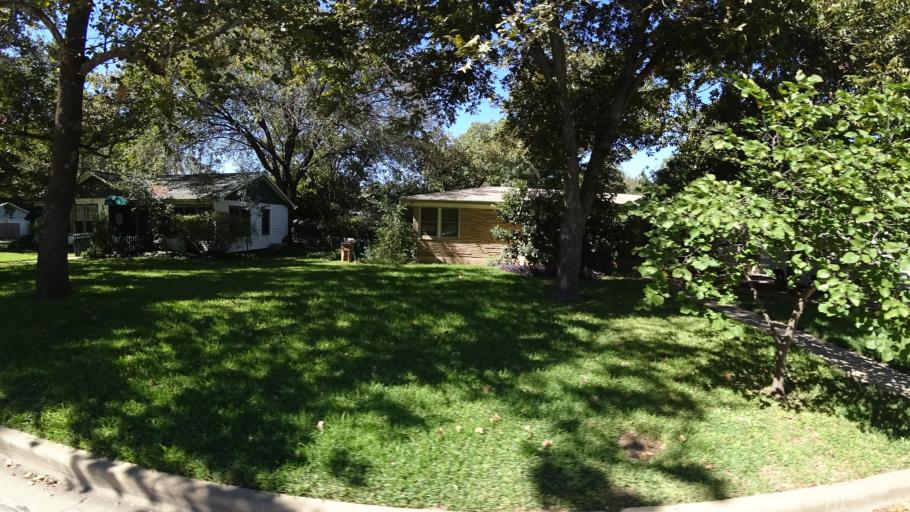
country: US
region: Texas
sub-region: Travis County
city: Austin
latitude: 30.3356
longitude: -97.7429
